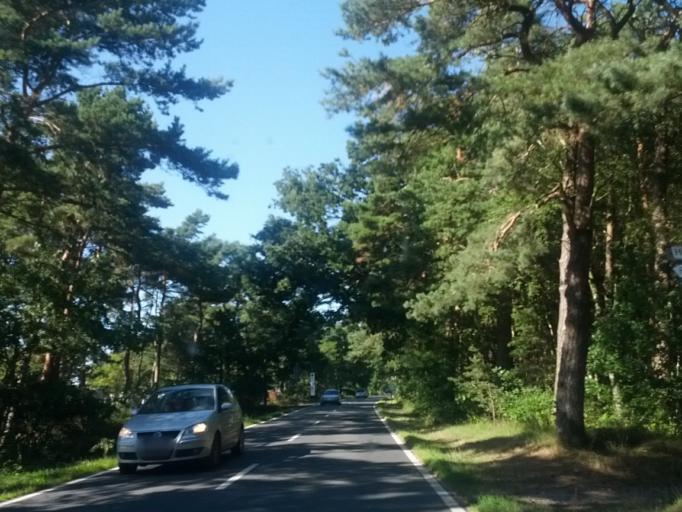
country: DE
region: Mecklenburg-Vorpommern
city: Ostseebad Gohren
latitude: 54.2832
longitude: 13.7139
